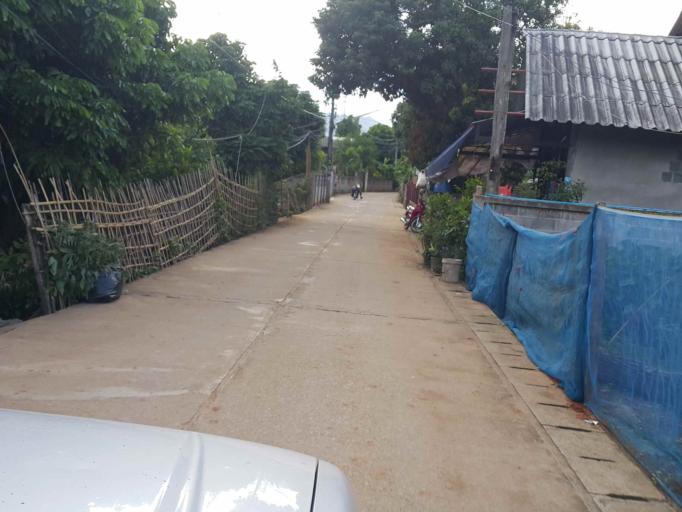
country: TH
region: Chiang Mai
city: Mae Chaem
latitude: 18.4972
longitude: 98.3702
